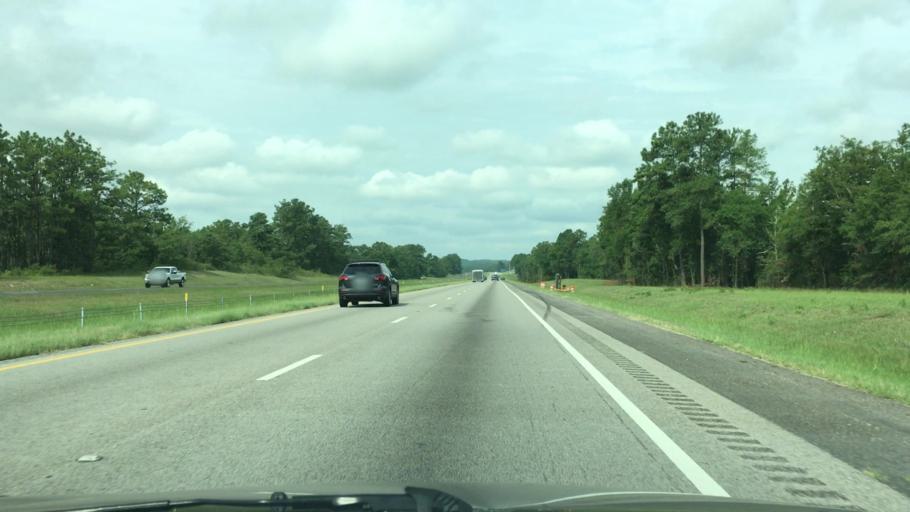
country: US
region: South Carolina
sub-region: Aiken County
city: Aiken
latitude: 33.6582
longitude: -81.6936
